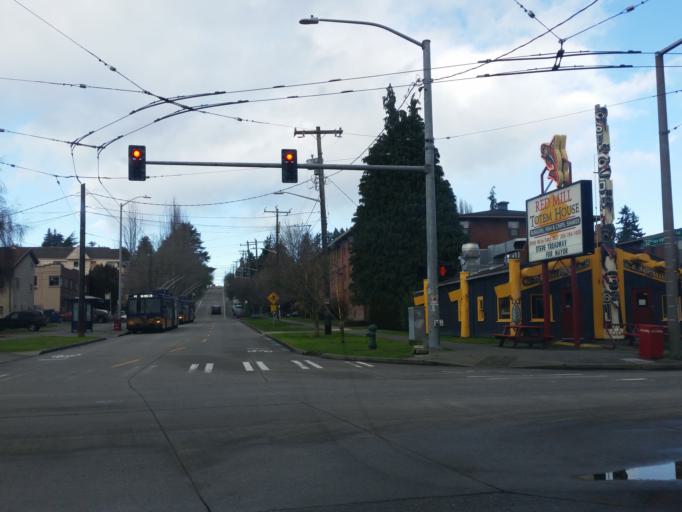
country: US
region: Washington
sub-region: King County
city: Seattle
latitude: 47.6674
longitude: -122.3983
